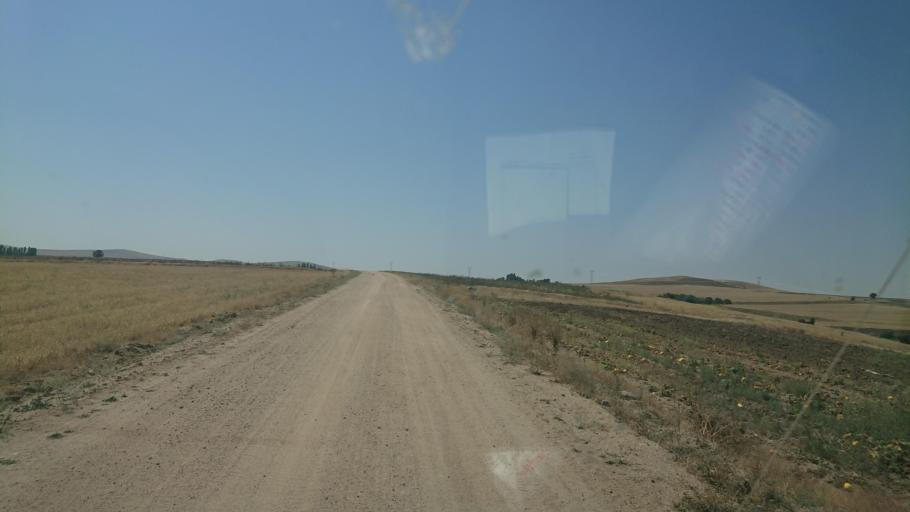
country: TR
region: Aksaray
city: Agacoren
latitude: 38.8141
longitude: 33.9538
